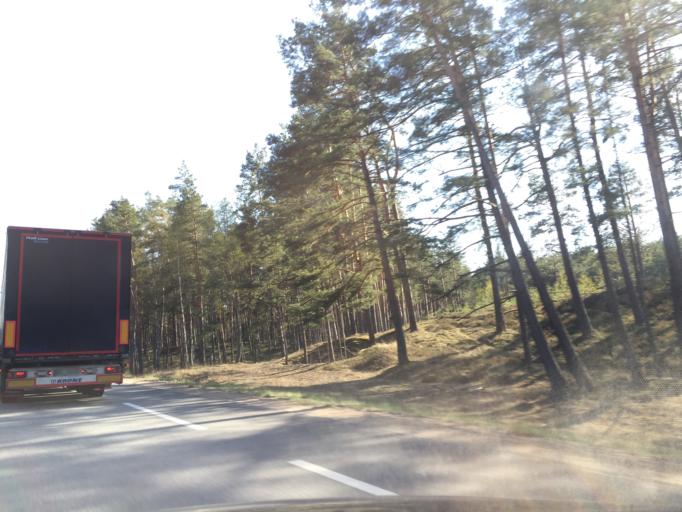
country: LV
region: Carnikava
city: Carnikava
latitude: 57.1757
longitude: 24.3424
